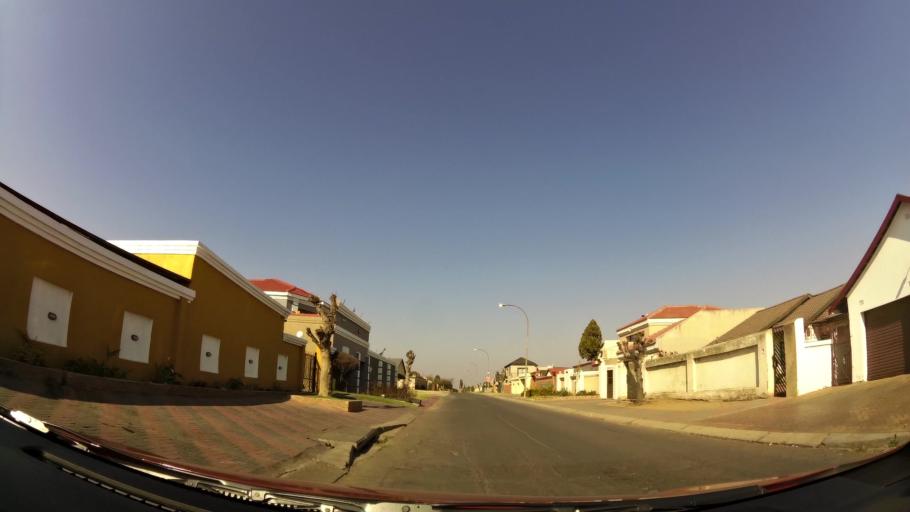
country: ZA
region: Gauteng
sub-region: City of Johannesburg Metropolitan Municipality
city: Johannesburg
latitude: -26.2467
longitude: 27.9555
